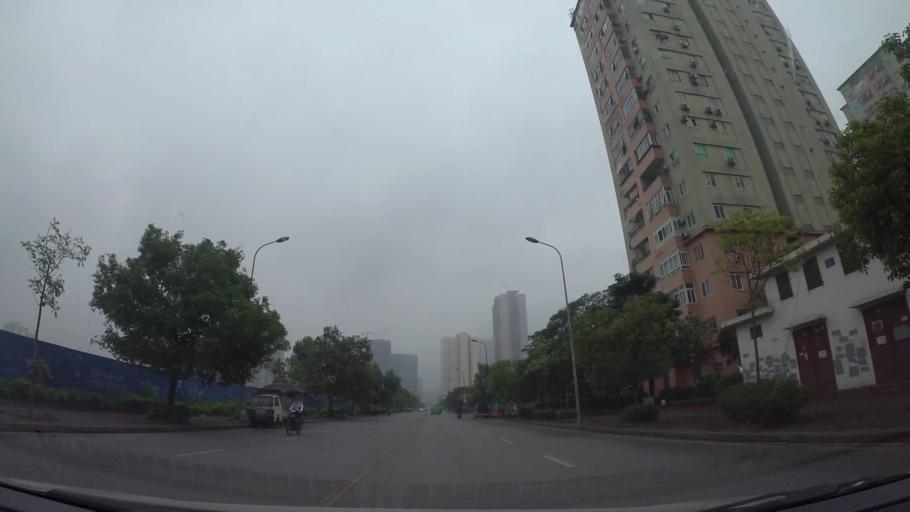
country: VN
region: Ha Noi
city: Thanh Xuan
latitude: 21.0135
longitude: 105.7911
